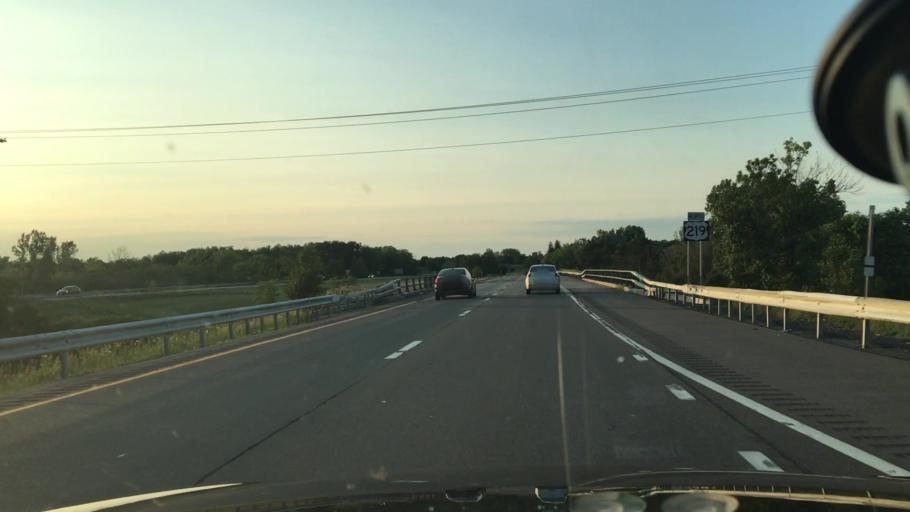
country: US
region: New York
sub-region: Erie County
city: Orchard Park
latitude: 42.7959
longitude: -78.7758
